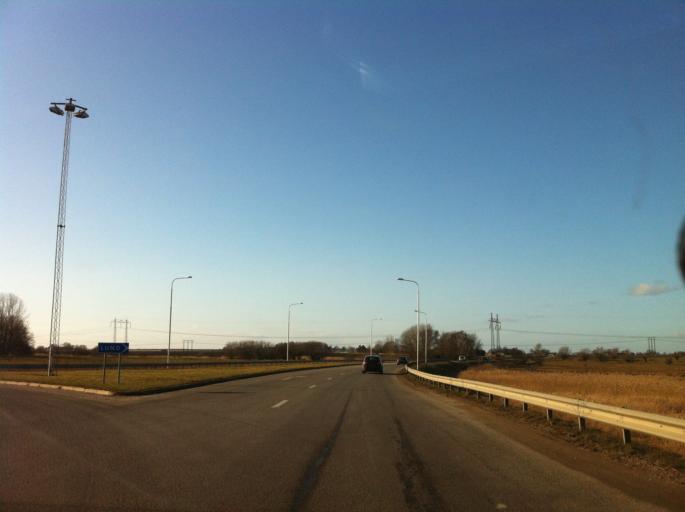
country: SE
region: Skane
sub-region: Svedala Kommun
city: Klagerup
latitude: 55.5641
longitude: 13.2553
